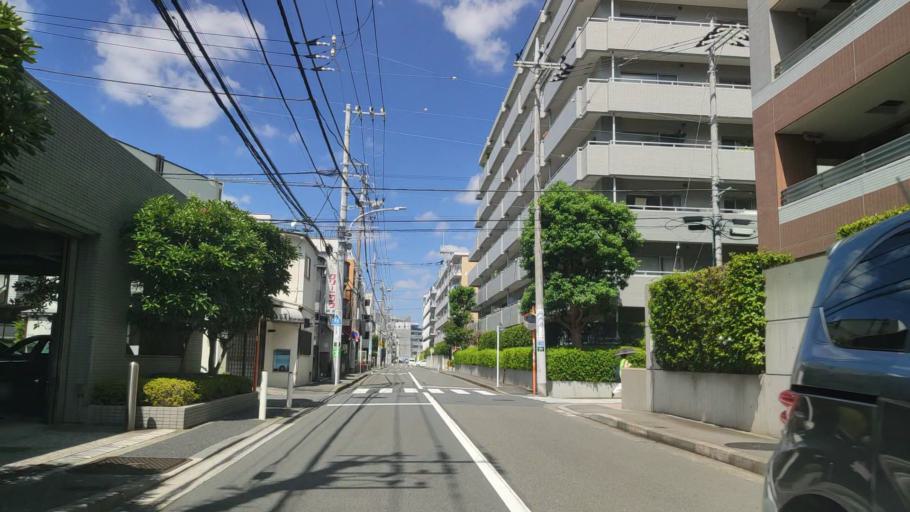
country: JP
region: Kanagawa
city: Yokohama
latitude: 35.5224
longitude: 139.6227
